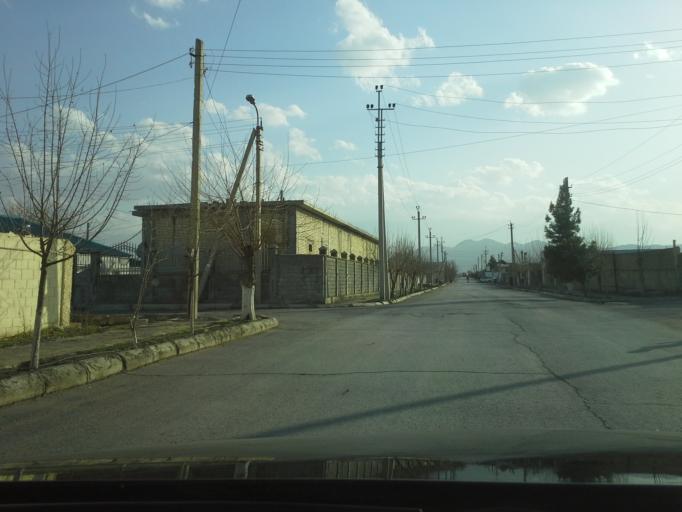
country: TM
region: Ahal
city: Abadan
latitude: 38.0209
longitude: 58.2320
